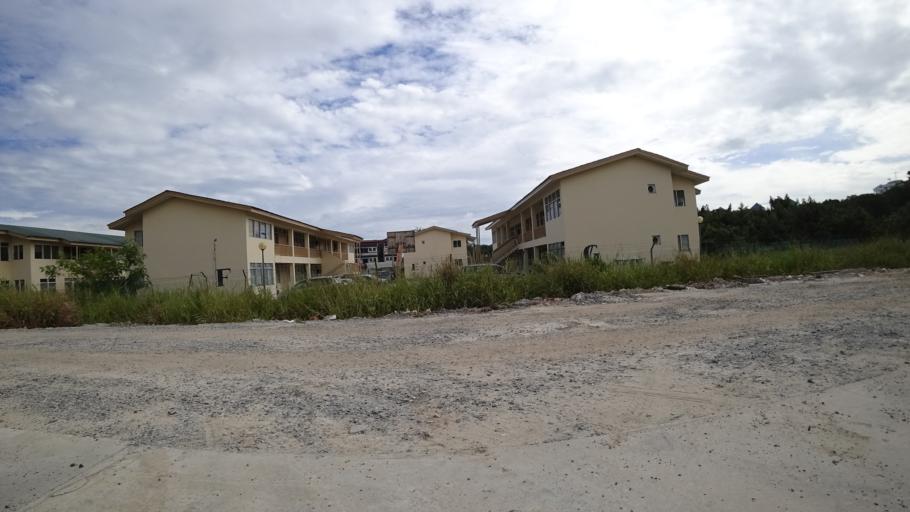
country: BN
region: Brunei and Muara
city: Bandar Seri Begawan
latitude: 4.8996
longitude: 114.9301
